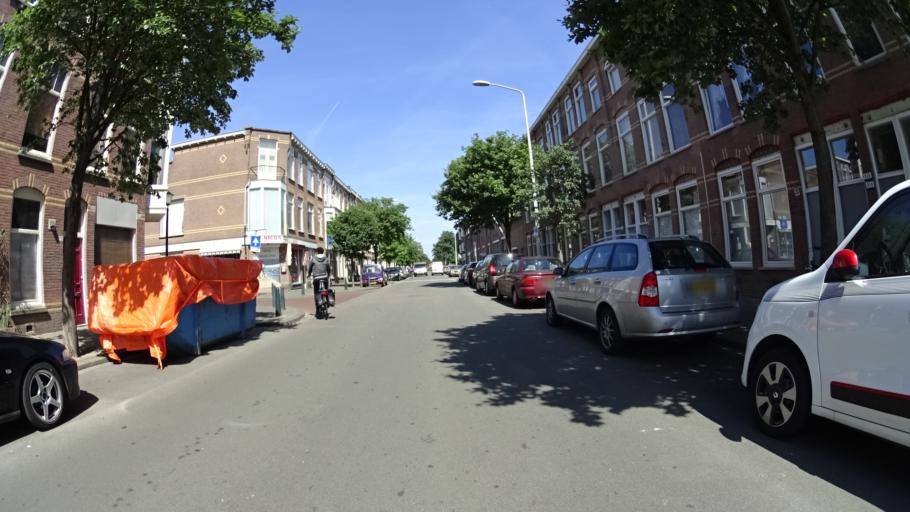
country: NL
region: South Holland
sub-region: Gemeente Den Haag
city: The Hague
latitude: 52.0734
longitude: 4.2745
